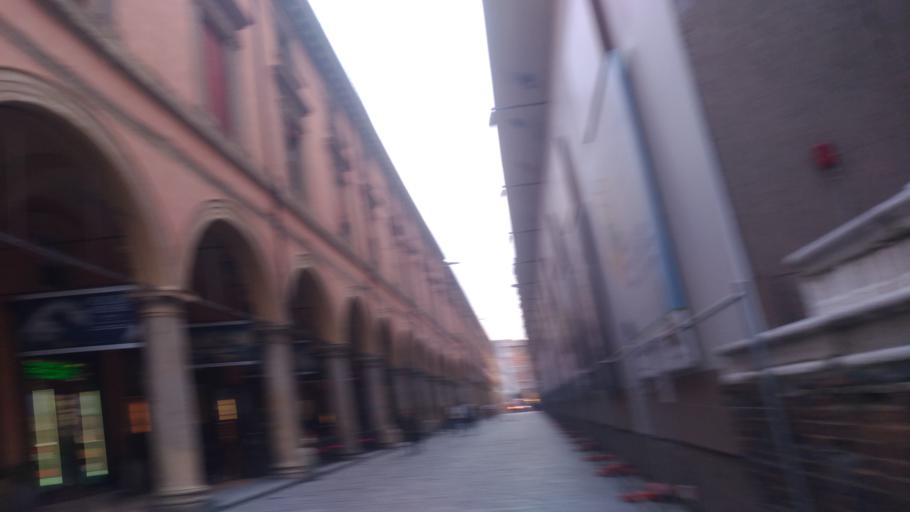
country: IT
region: Emilia-Romagna
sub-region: Provincia di Bologna
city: Bologna
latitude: 44.4933
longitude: 11.3437
